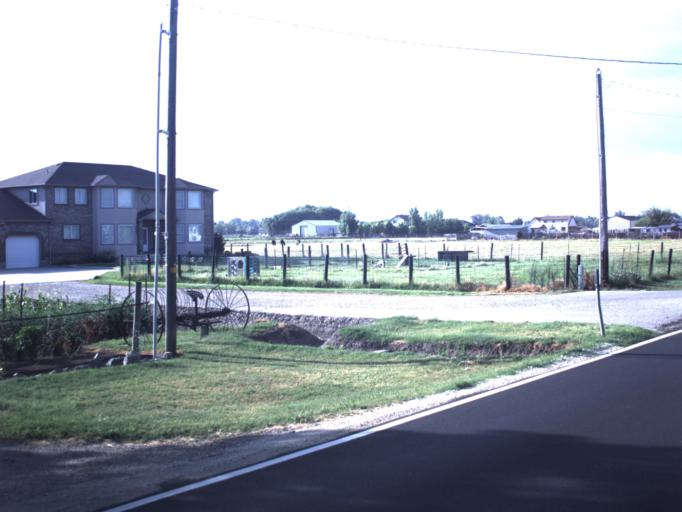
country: US
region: Utah
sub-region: Weber County
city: West Haven
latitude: 41.2306
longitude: -112.0928
